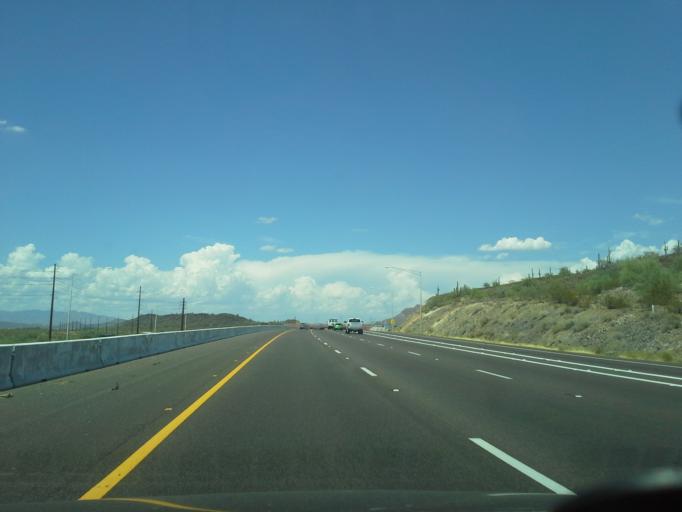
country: US
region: Arizona
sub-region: Maricopa County
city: Anthem
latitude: 33.8348
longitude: -112.1448
